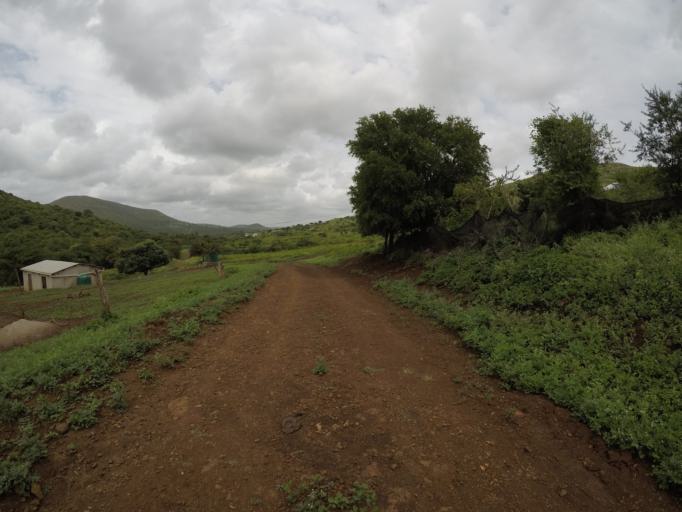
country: ZA
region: KwaZulu-Natal
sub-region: uThungulu District Municipality
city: Empangeni
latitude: -28.5818
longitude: 31.8889
